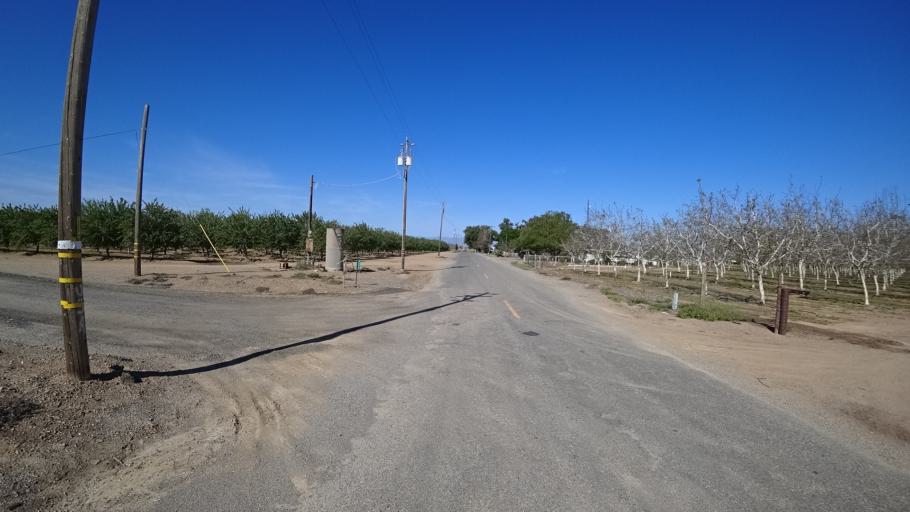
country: US
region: California
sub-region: Glenn County
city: Willows
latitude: 39.6113
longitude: -122.1835
